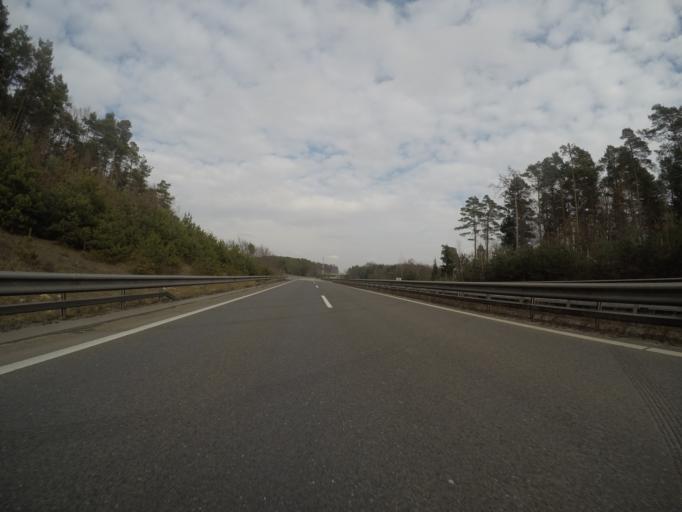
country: SI
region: Sveti Jurij
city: Sveti Jurij ob Scavnici
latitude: 46.5769
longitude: 16.0598
